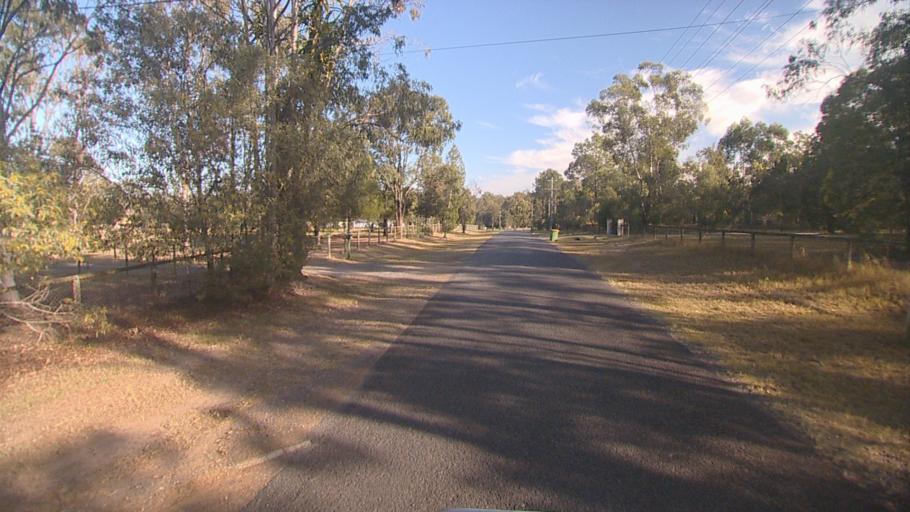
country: AU
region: Queensland
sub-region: Logan
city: North Maclean
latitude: -27.7606
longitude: 153.0016
